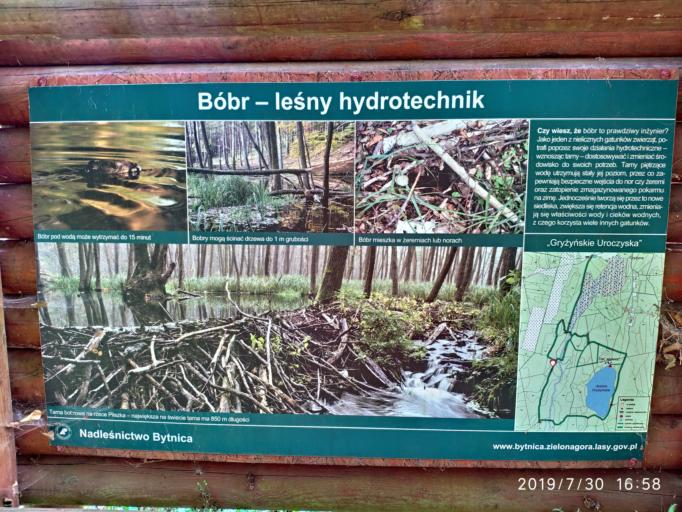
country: PL
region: Lubusz
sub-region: Powiat krosnienski
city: Bytnica
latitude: 52.1685
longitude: 15.2690
